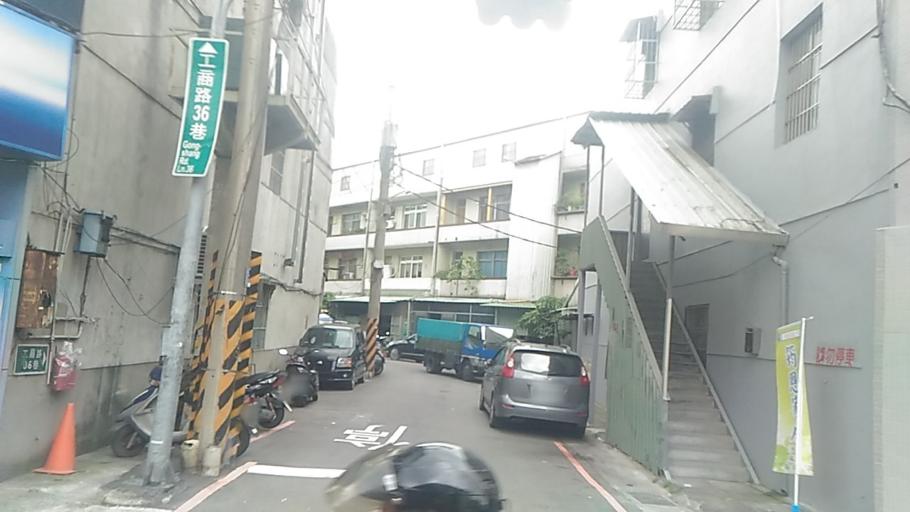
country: TW
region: Taipei
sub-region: Taipei
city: Banqiao
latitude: 25.0837
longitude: 121.4396
